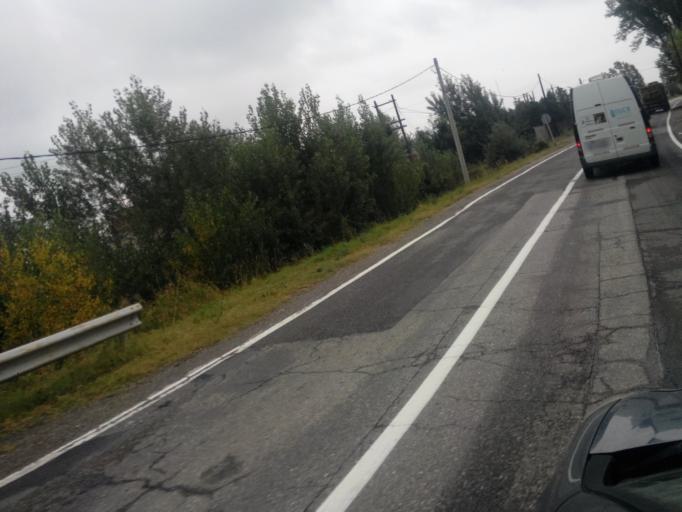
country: RO
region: Cluj
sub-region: Comuna Moldovenesti
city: Moldovenesti
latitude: 46.5114
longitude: 23.6623
